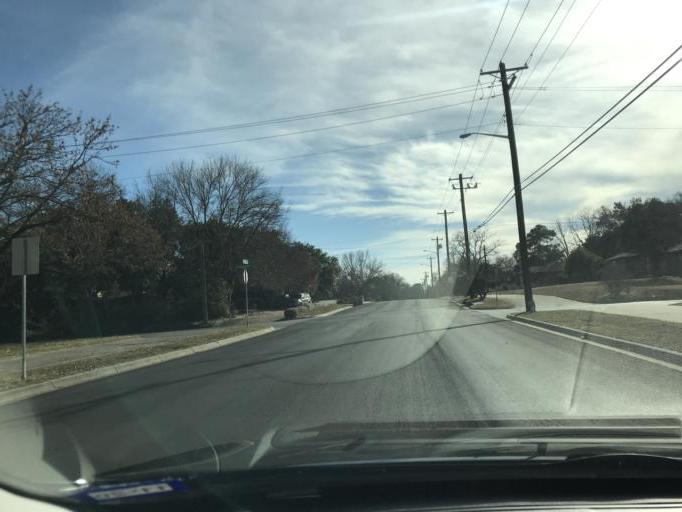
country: US
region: Texas
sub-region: Denton County
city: Denton
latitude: 33.2220
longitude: -97.1551
